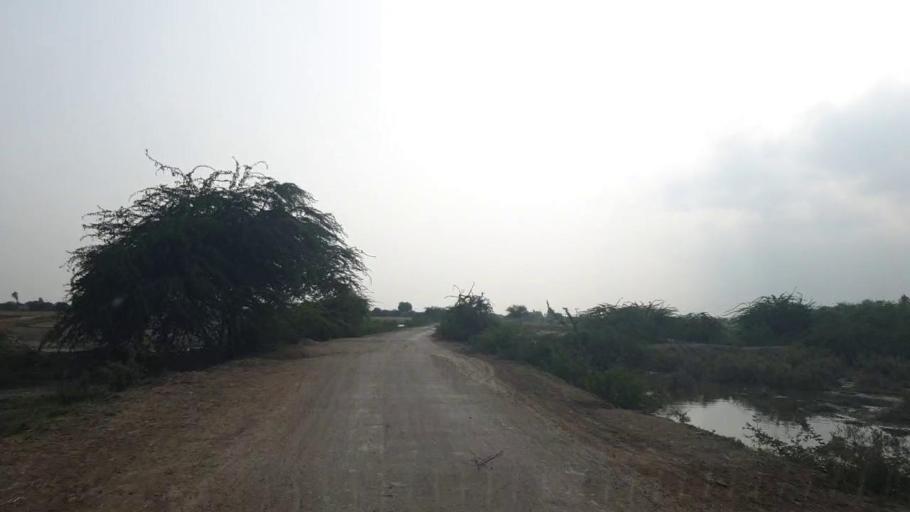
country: PK
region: Sindh
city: Badin
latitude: 24.6264
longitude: 68.6910
